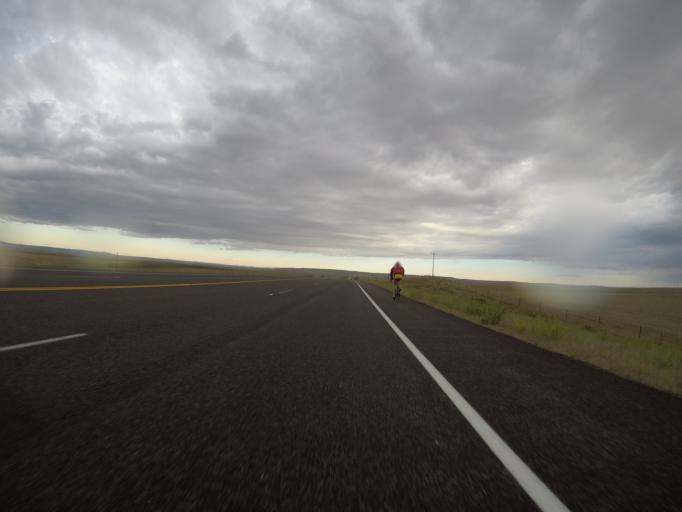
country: US
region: Wyoming
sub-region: Albany County
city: Laramie
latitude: 41.8336
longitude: -106.0185
